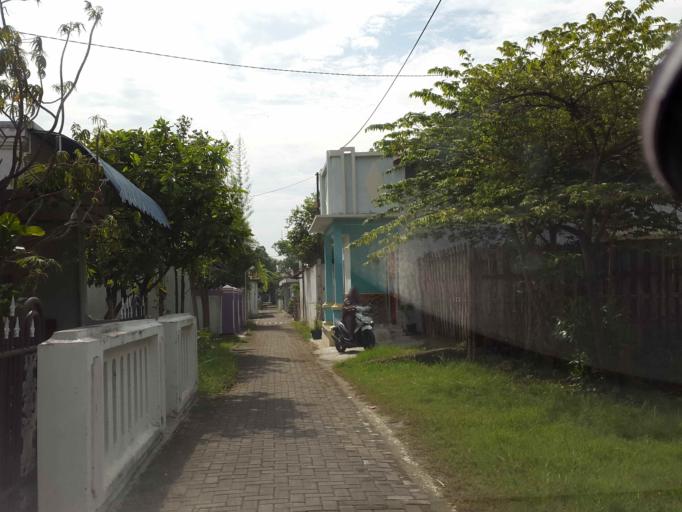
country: ID
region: Central Java
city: Dukuhturi
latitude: -6.8730
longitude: 109.0534
